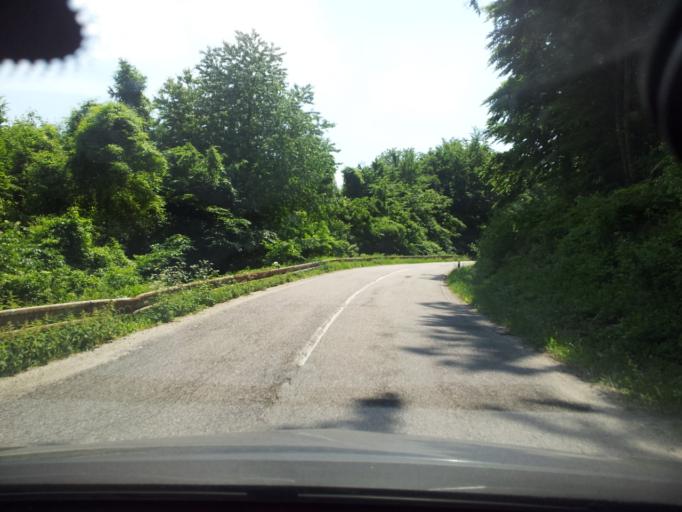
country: SK
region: Nitriansky
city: Partizanske
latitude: 48.5780
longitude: 18.4542
